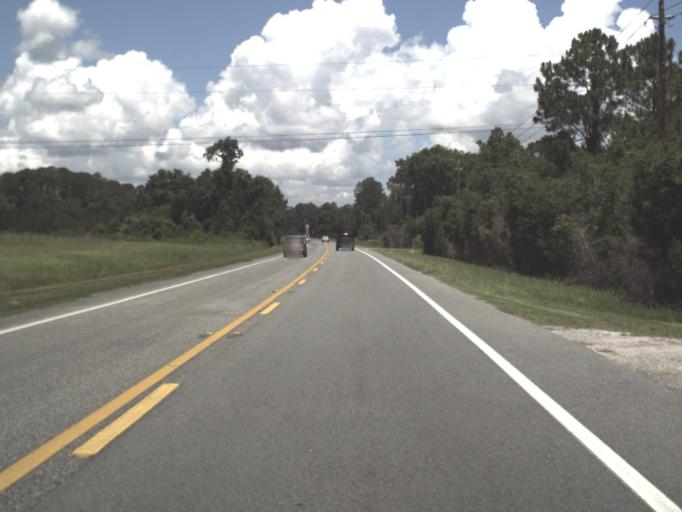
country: US
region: Florida
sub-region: Putnam County
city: Crescent City
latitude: 29.4766
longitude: -81.5395
